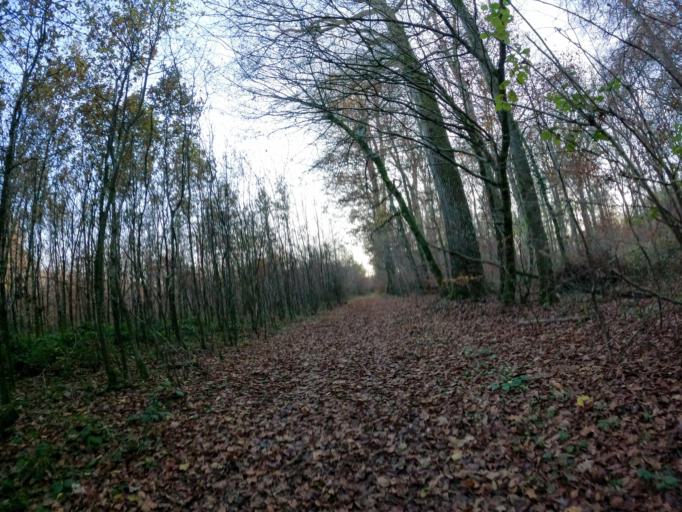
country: LU
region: Luxembourg
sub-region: Canton de Capellen
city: Dippach
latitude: 49.6027
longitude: 6.0059
